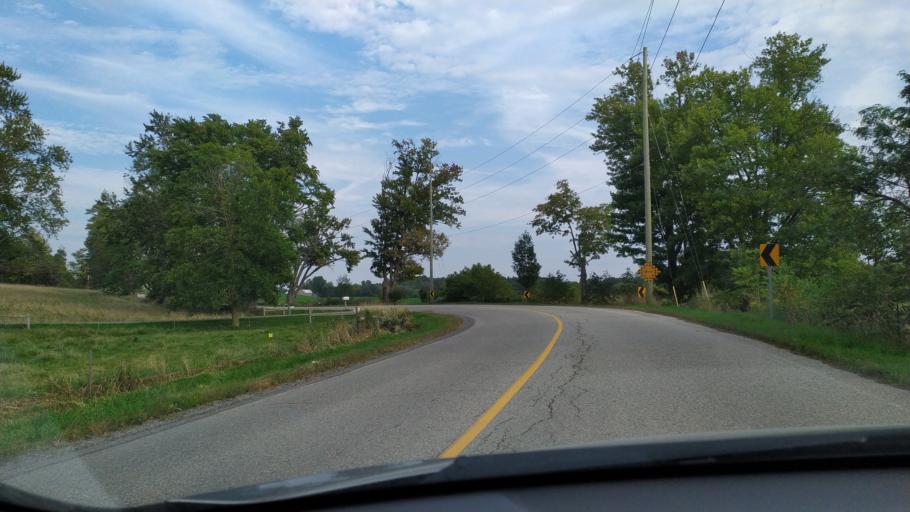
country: CA
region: Ontario
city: Stratford
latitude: 43.4692
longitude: -80.7828
